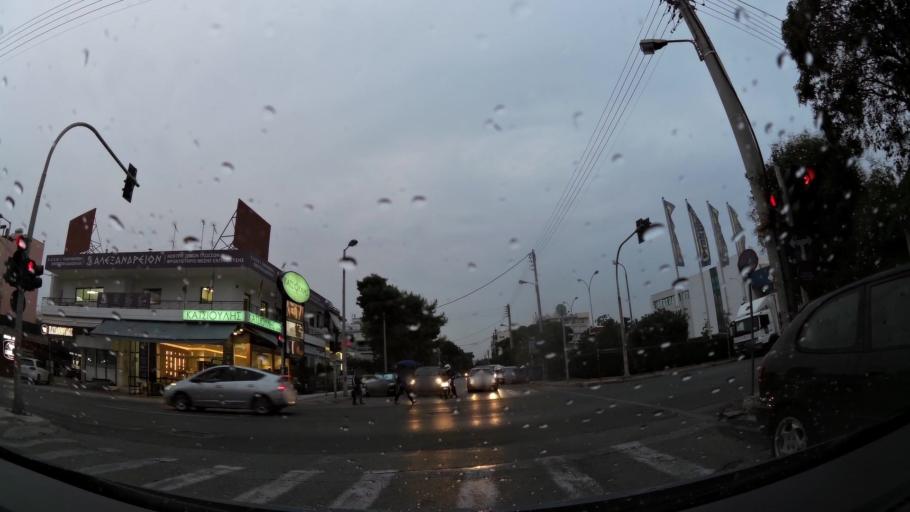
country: GR
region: Attica
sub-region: Nomarchia Athinas
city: Argyroupoli
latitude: 37.9061
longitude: 23.7435
